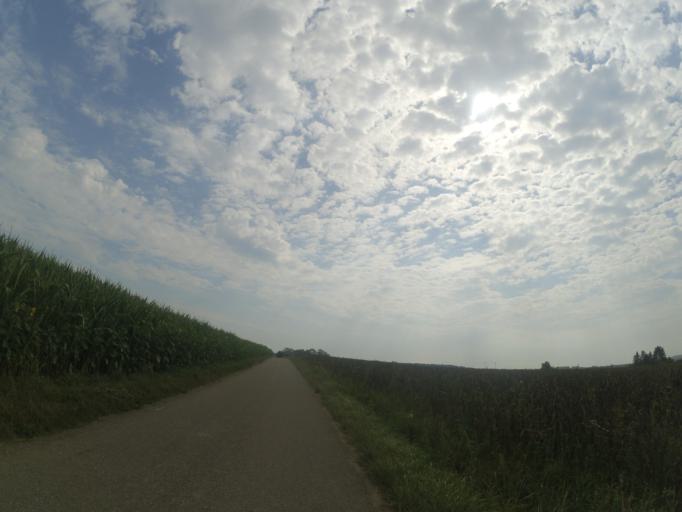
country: DE
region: Baden-Wuerttemberg
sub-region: Tuebingen Region
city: Dornstadt
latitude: 48.4820
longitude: 9.9189
